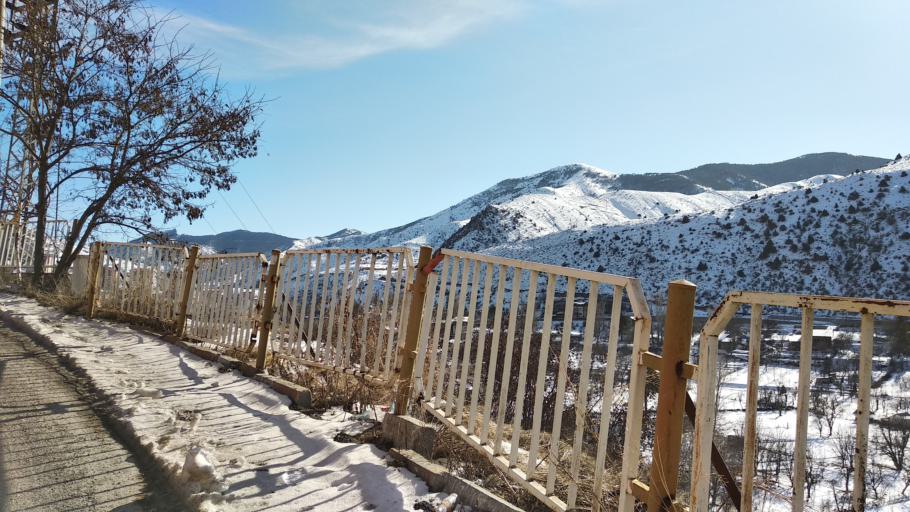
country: TR
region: Gumushane
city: Gumushkhane
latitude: 40.4371
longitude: 39.5091
